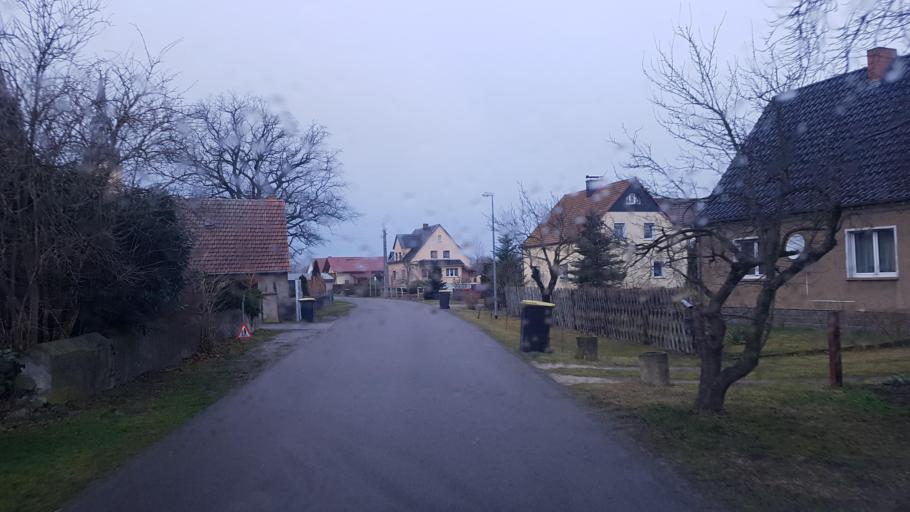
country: DE
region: Brandenburg
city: Kroppen
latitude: 51.3857
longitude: 13.8014
